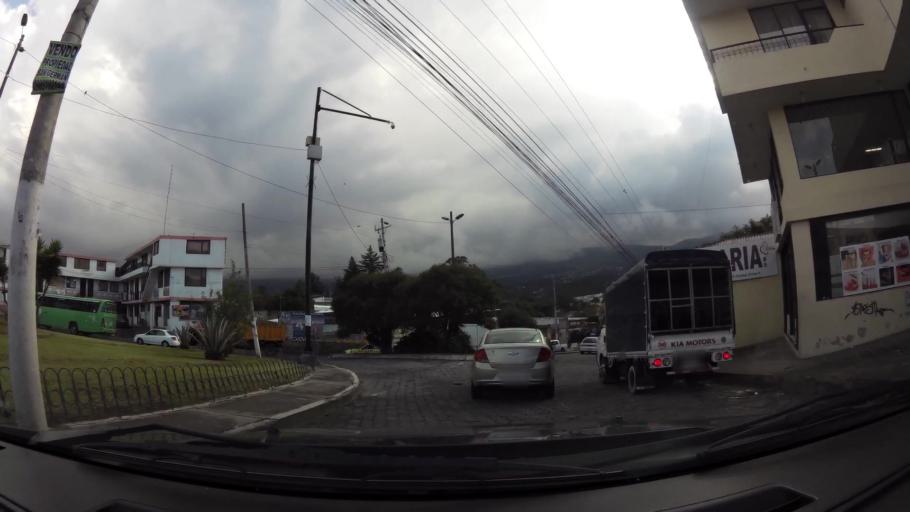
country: EC
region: Pichincha
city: Sangolqui
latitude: -0.2929
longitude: -78.4789
